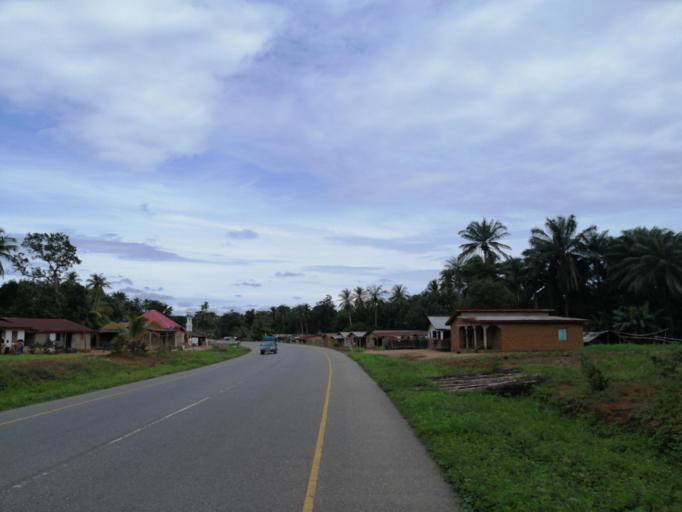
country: SL
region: Northern Province
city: Port Loko
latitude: 8.7651
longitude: -12.9056
